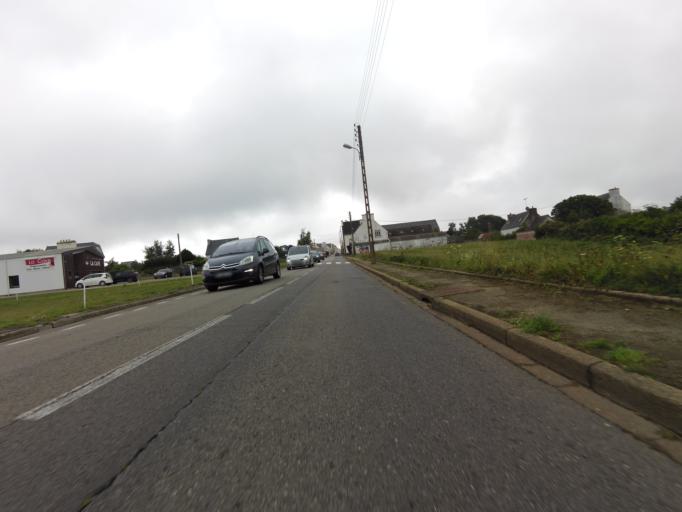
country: FR
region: Brittany
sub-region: Departement du Finistere
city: Plouhinec
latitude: 48.0155
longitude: -4.4962
